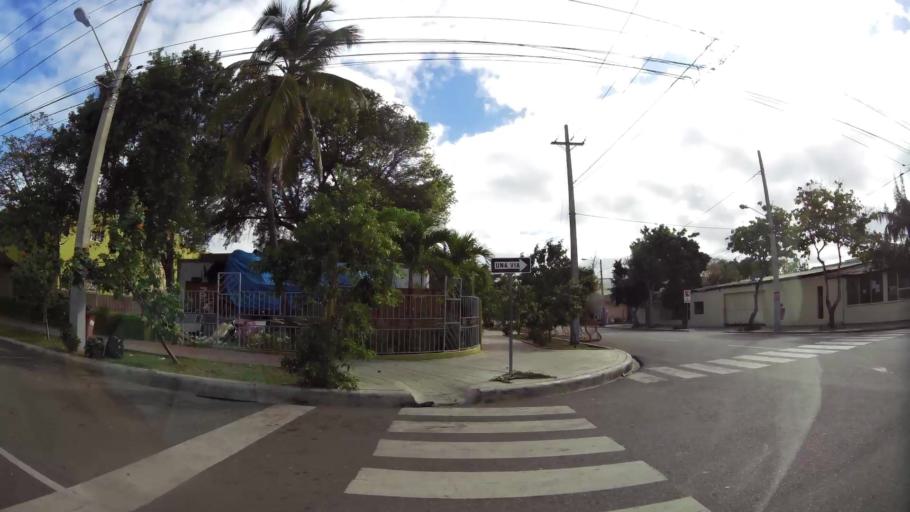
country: DO
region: Nacional
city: La Julia
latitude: 18.4503
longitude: -69.9254
